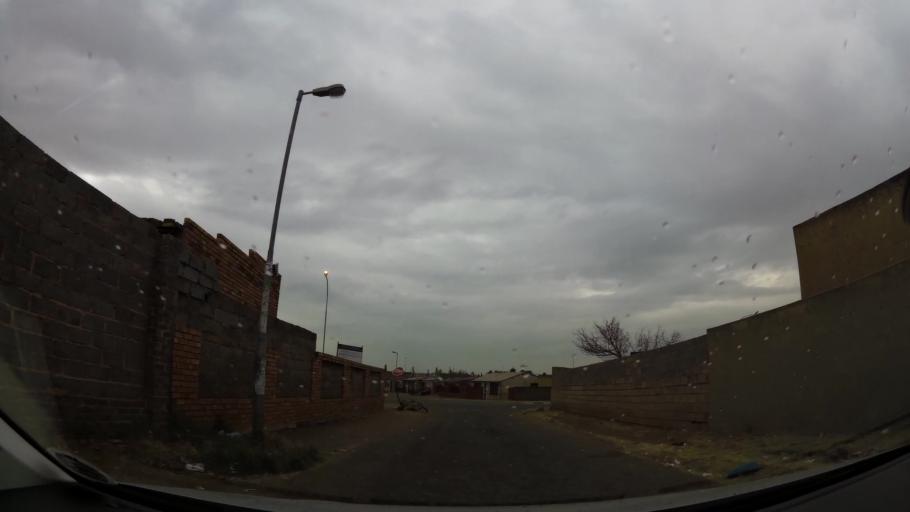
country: ZA
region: Gauteng
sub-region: City of Johannesburg Metropolitan Municipality
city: Soweto
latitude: -26.2544
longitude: 27.8640
